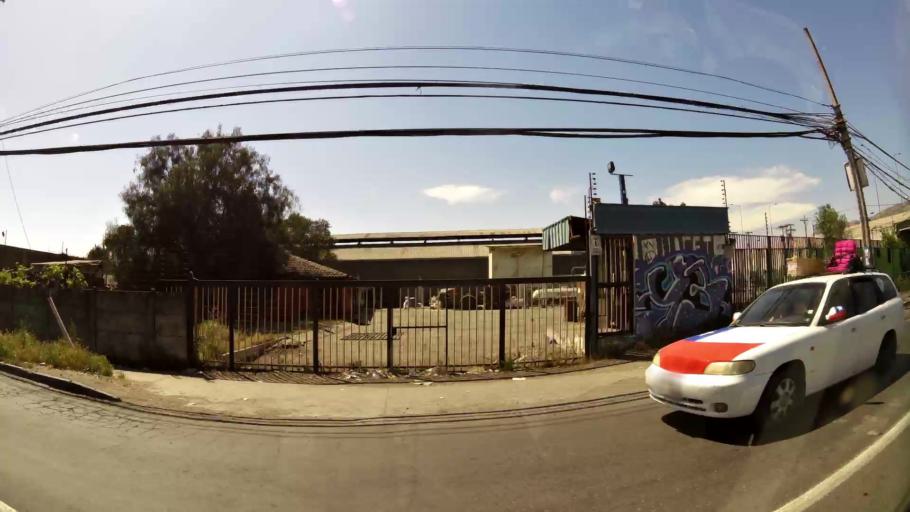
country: CL
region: Santiago Metropolitan
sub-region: Provincia de Santiago
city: Lo Prado
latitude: -33.3862
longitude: -70.7608
